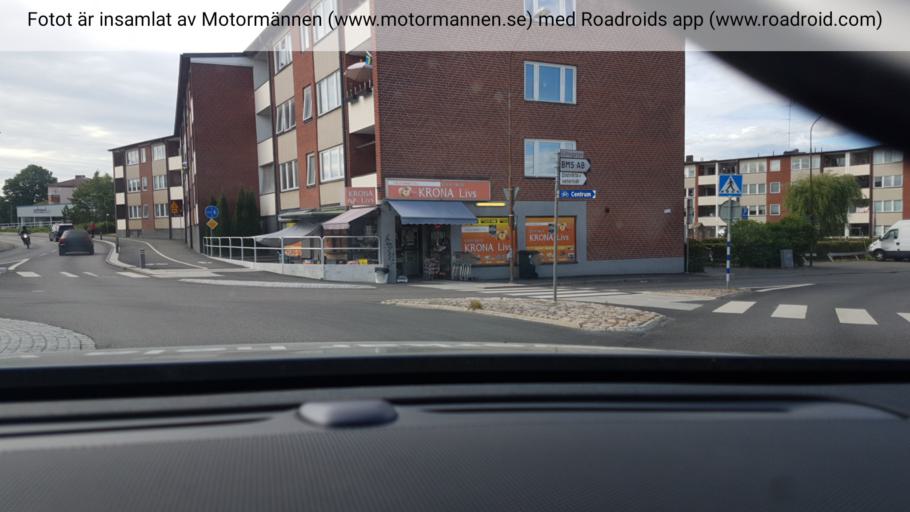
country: SE
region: Skane
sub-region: Hassleholms Kommun
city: Hassleholm
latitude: 56.1614
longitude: 13.7633
